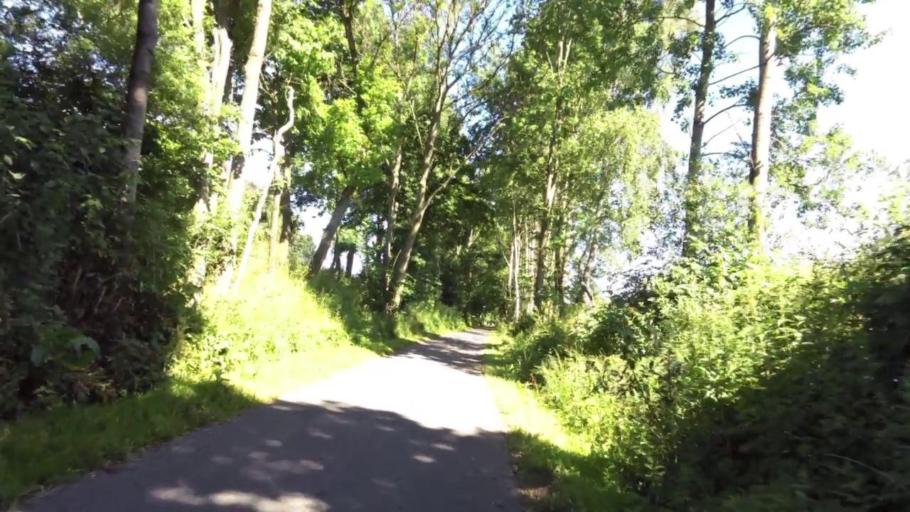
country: PL
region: West Pomeranian Voivodeship
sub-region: Powiat bialogardzki
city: Karlino
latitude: 54.0600
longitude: 15.8513
